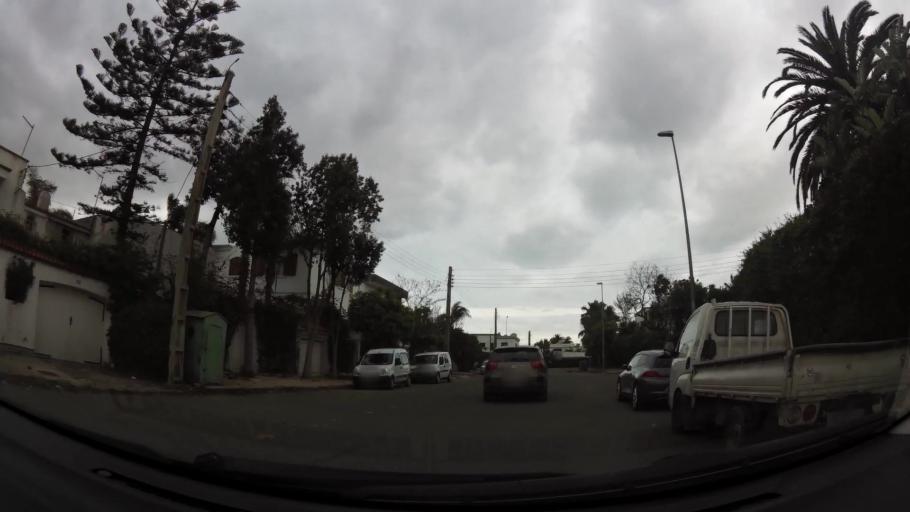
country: MA
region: Grand Casablanca
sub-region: Casablanca
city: Casablanca
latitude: 33.5699
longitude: -7.6602
